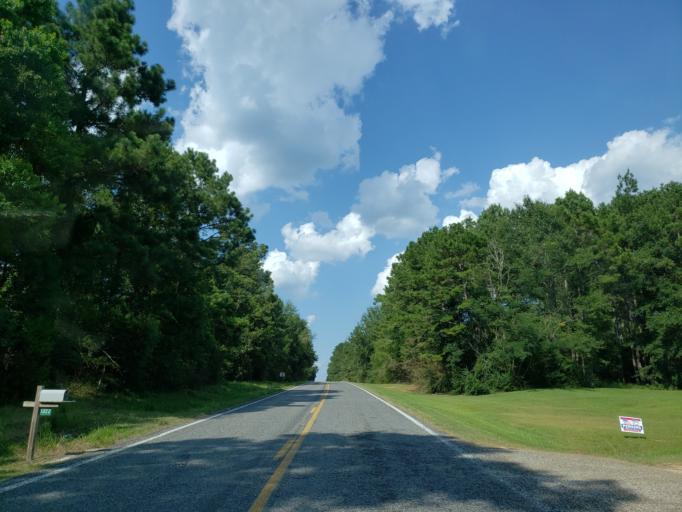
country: US
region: Mississippi
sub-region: Covington County
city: Collins
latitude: 31.6062
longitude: -89.4373
